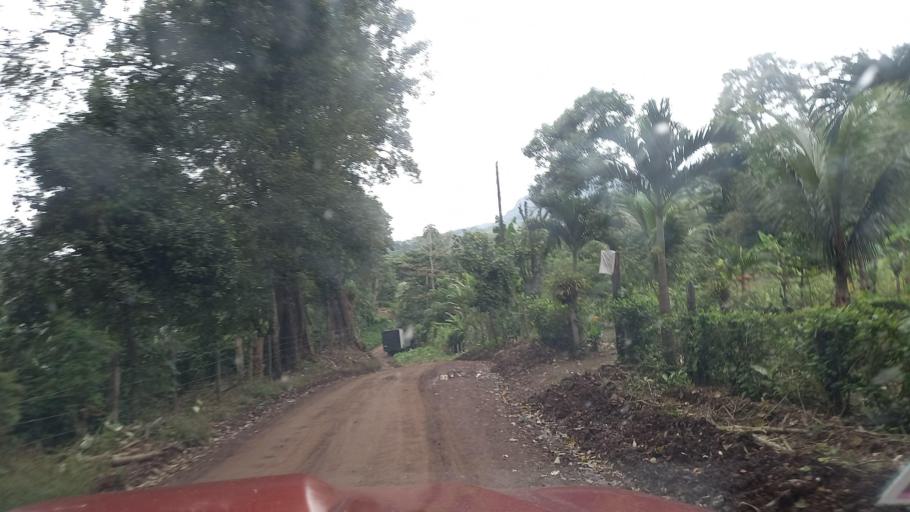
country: NI
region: Jinotega
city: San Jose de Bocay
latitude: 13.3519
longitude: -85.6624
